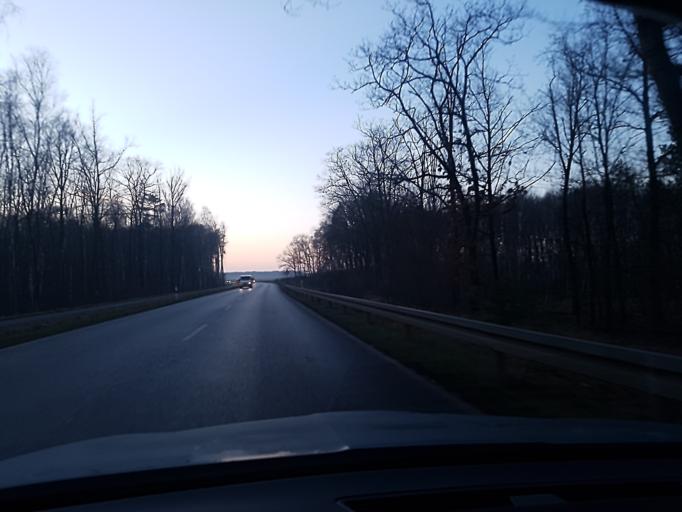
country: DE
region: Brandenburg
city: Finsterwalde
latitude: 51.6336
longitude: 13.6842
